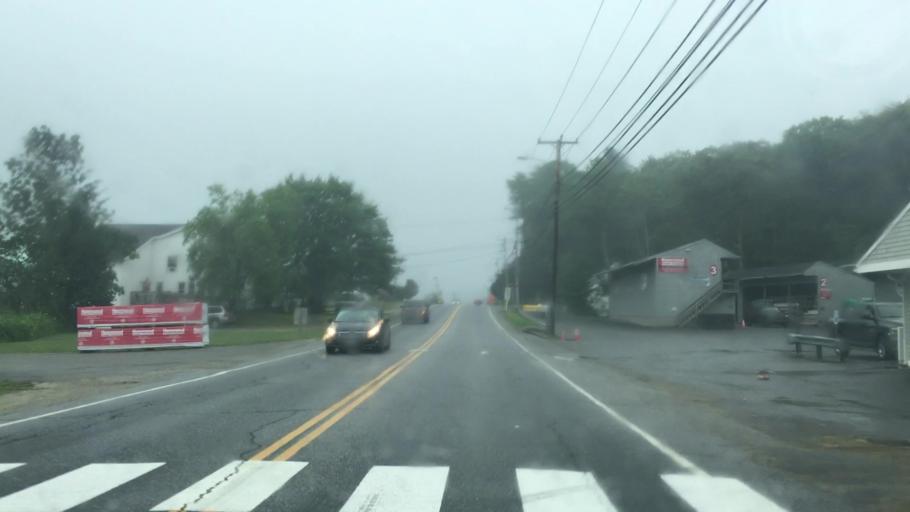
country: US
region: Maine
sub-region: Lincoln County
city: Boothbay
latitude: 43.8669
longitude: -69.6294
